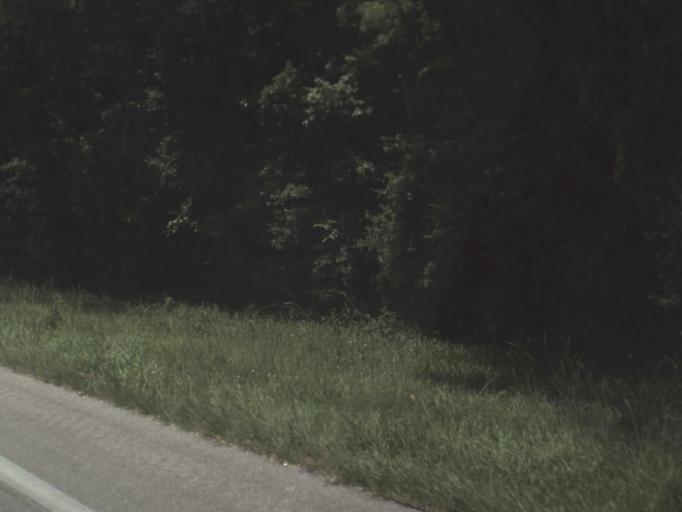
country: US
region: Florida
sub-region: Gilchrist County
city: Trenton
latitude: 29.6290
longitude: -82.8234
